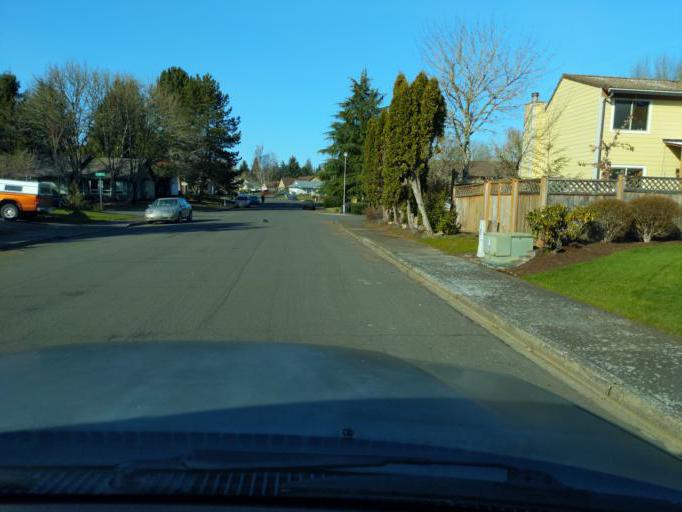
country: US
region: Oregon
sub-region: Yamhill County
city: McMinnville
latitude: 45.1989
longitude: -123.2122
